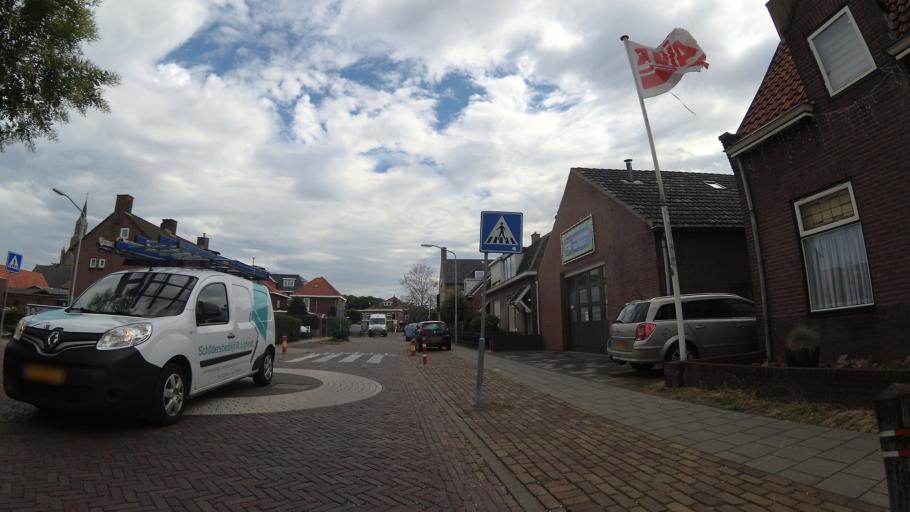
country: NL
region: North Brabant
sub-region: Gemeente Made en Drimmelen
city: Made
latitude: 51.6811
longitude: 4.7923
